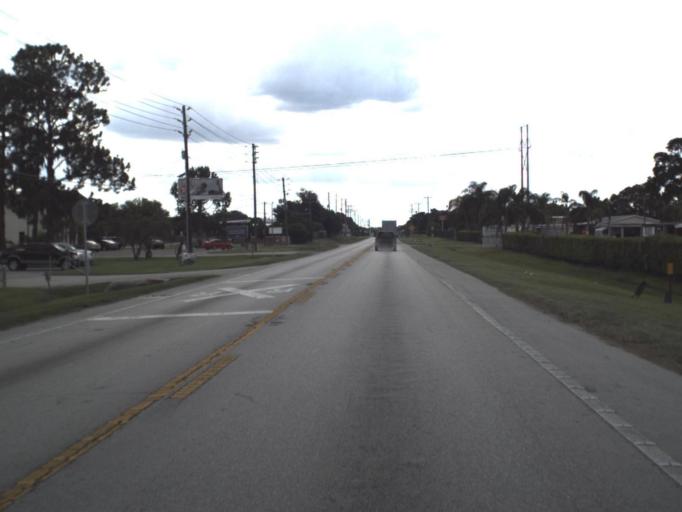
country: US
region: Florida
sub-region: Polk County
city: Winston
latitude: 28.0373
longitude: -82.0106
